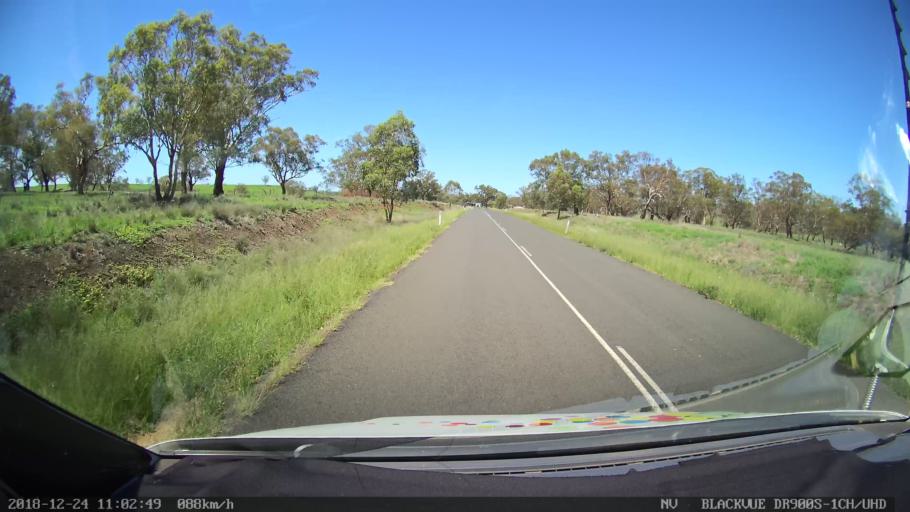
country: AU
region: New South Wales
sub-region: Upper Hunter Shire
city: Merriwa
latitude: -32.0892
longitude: 150.3719
